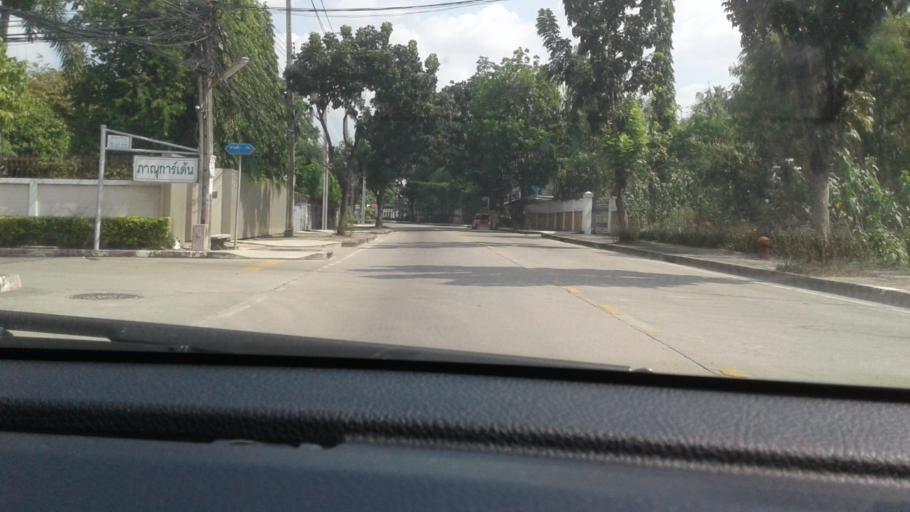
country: TH
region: Bangkok
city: Taling Chan
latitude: 13.7893
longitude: 100.4051
